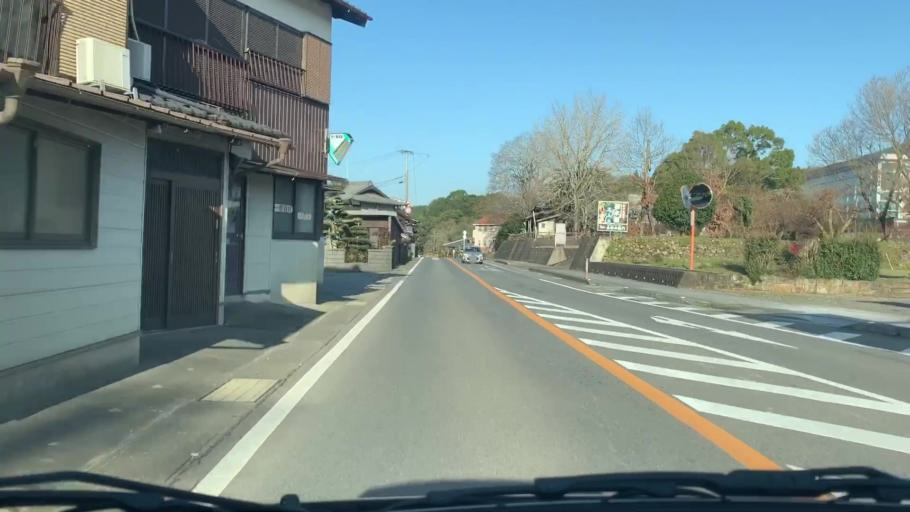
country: JP
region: Saga Prefecture
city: Takeocho-takeo
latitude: 33.2520
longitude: 129.9949
